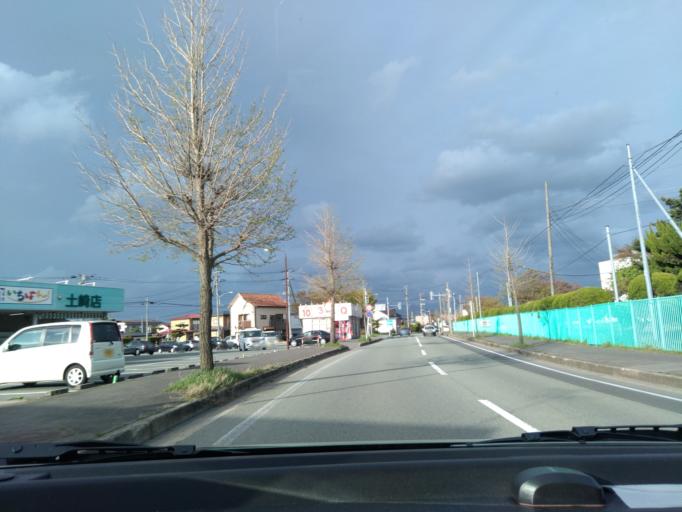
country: JP
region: Akita
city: Akita Shi
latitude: 39.7577
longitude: 140.0779
